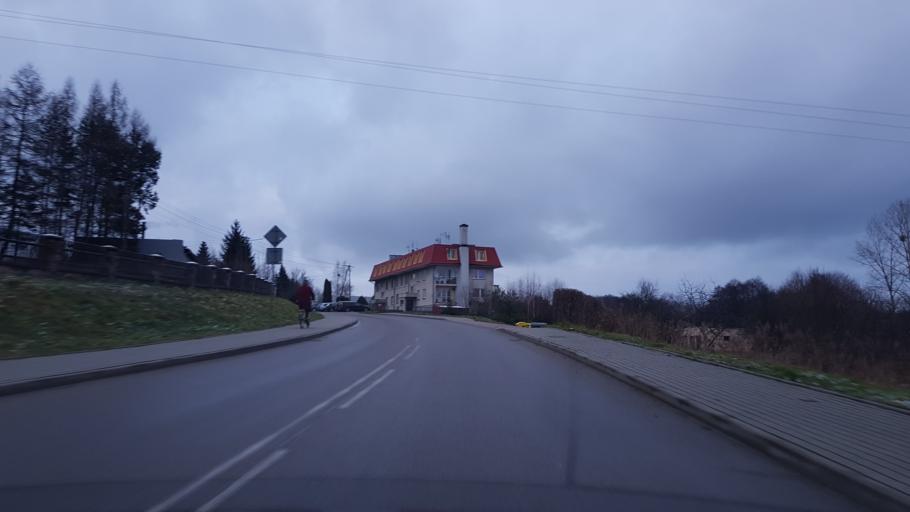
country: PL
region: Pomeranian Voivodeship
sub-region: Powiat bytowski
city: Tuchomie
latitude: 54.1175
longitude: 17.3360
